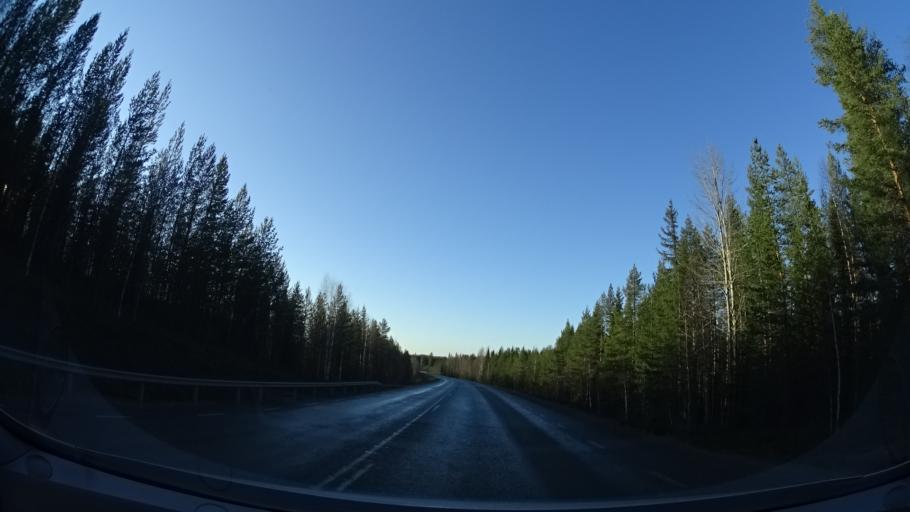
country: SE
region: Vaesterbotten
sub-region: Skelleftea Kommun
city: Langsele
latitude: 64.8882
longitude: 20.2694
